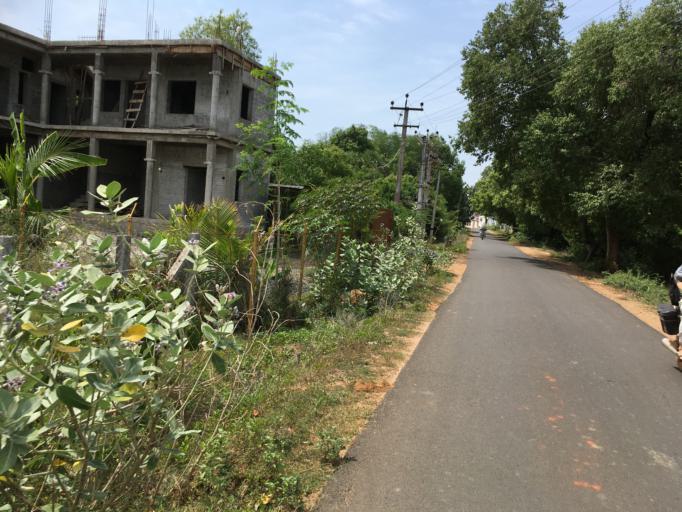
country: IN
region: Tamil Nadu
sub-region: Villupuram
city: Auroville
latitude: 12.0067
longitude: 79.7967
